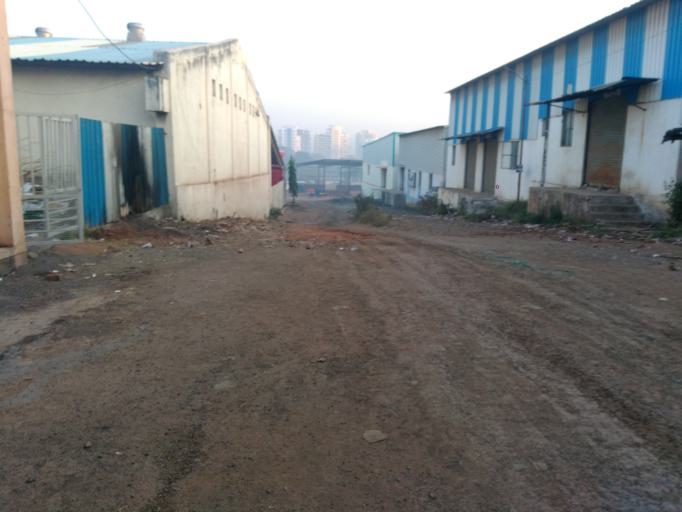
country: IN
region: Maharashtra
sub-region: Pune Division
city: Pune
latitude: 18.4540
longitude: 73.9003
